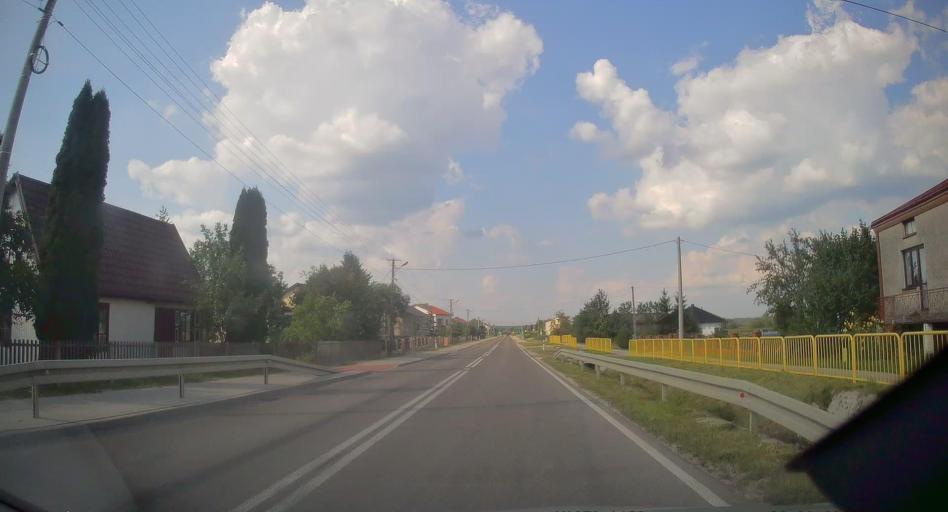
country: PL
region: Swietokrzyskie
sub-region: Powiat konecki
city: Radoszyce
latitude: 51.0399
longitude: 20.2826
